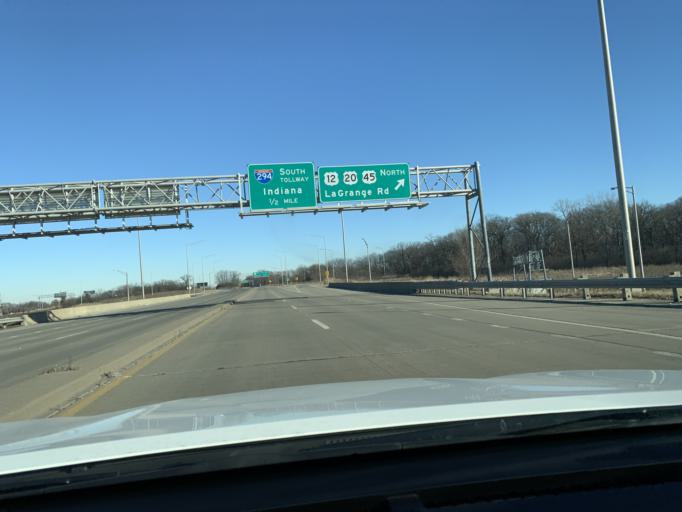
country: US
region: Illinois
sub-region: Cook County
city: Willow Springs
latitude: 41.7435
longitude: -87.8532
